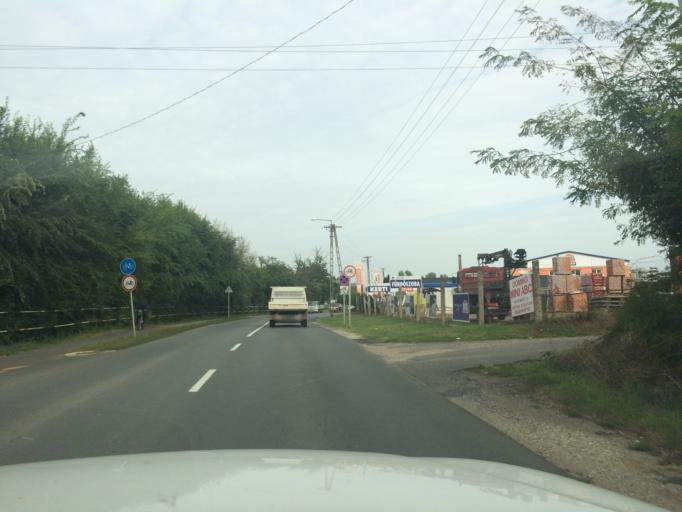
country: HU
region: Szabolcs-Szatmar-Bereg
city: Kotaj
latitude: 48.0123
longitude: 21.7387
